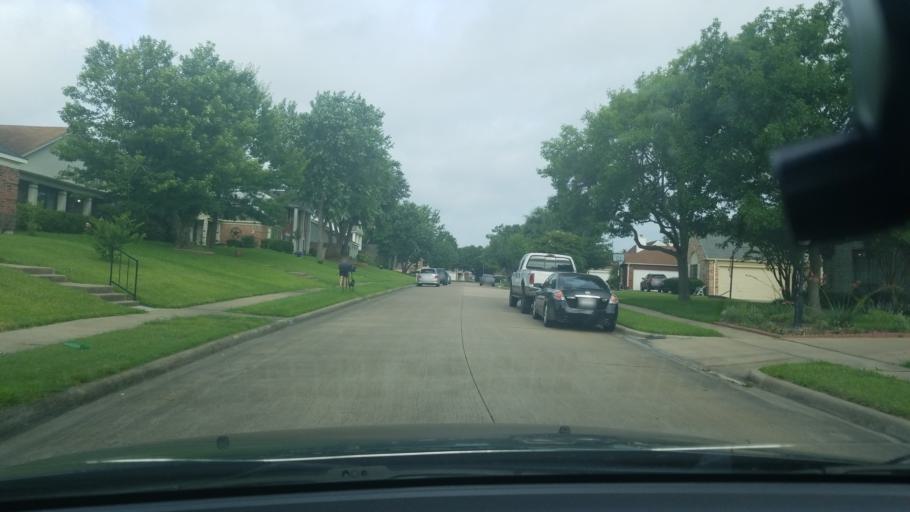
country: US
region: Texas
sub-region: Dallas County
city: Mesquite
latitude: 32.7893
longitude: -96.6482
